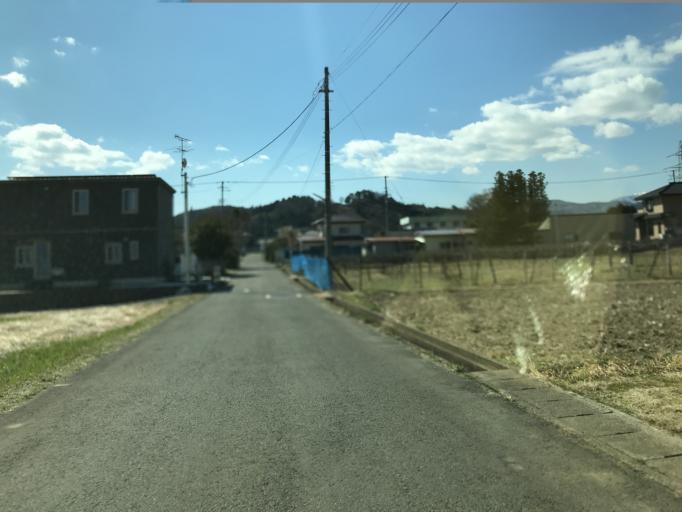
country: JP
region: Fukushima
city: Fukushima-shi
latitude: 37.7331
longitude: 140.4139
